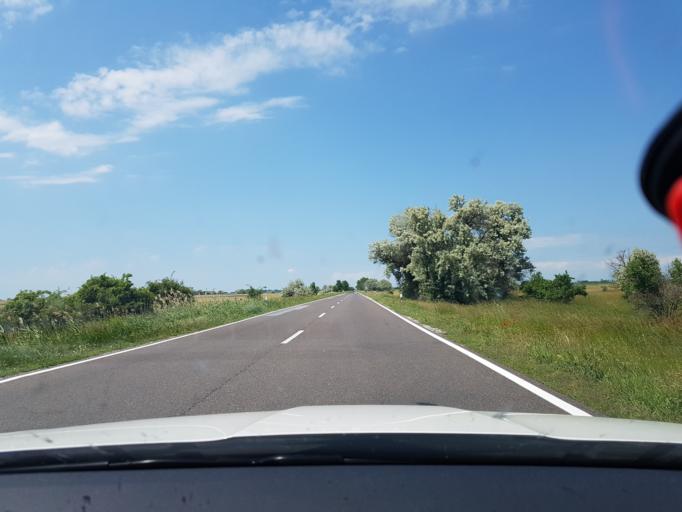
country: HU
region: Hajdu-Bihar
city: Egyek
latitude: 47.5467
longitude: 20.8935
